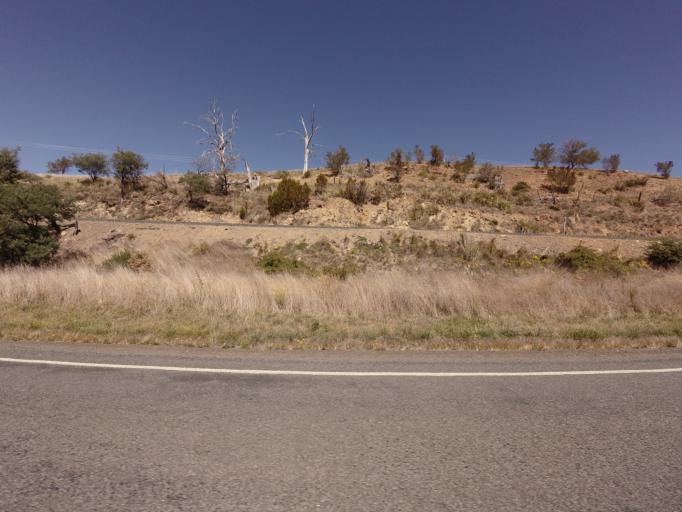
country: AU
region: Tasmania
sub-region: Northern Midlands
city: Evandale
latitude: -41.7341
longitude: 147.8172
